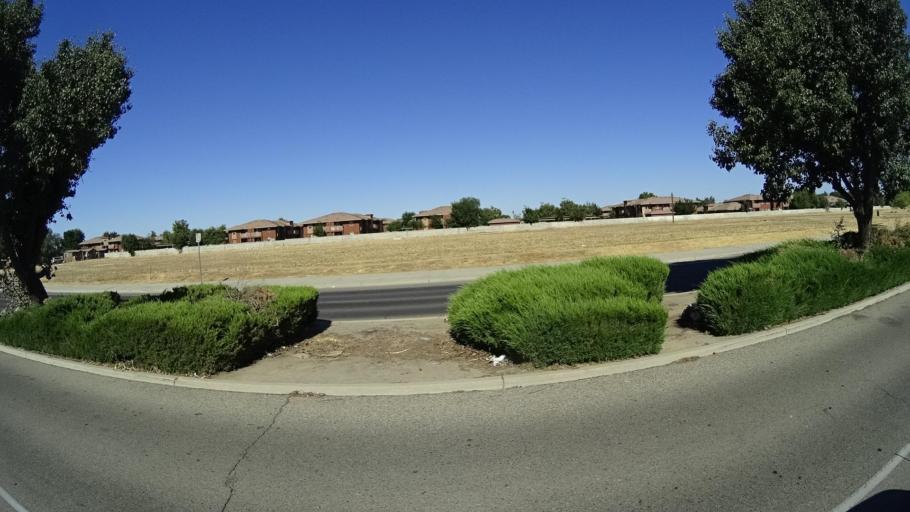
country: US
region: California
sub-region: Fresno County
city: Fresno
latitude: 36.7119
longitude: -119.7906
